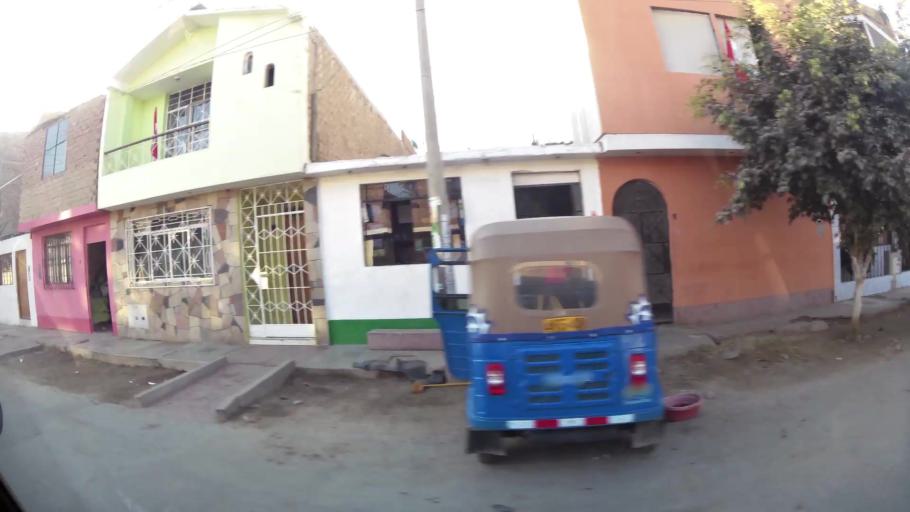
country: PE
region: Ica
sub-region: Provincia de Ica
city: Ica
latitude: -14.0581
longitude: -75.7298
